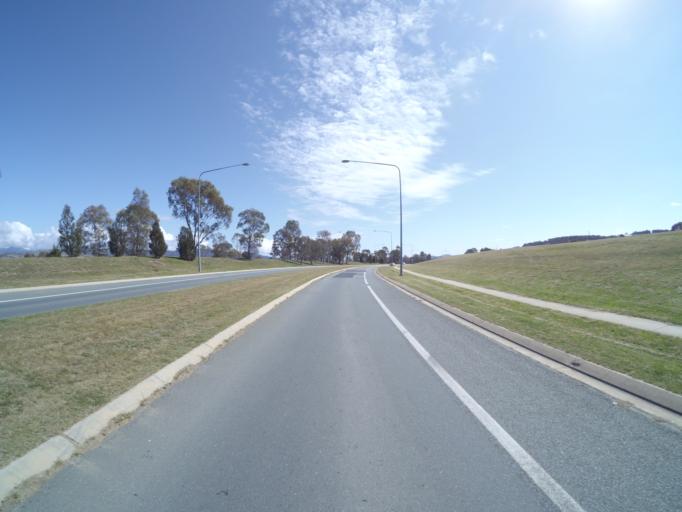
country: AU
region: Australian Capital Territory
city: Macarthur
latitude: -35.4491
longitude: 149.0802
